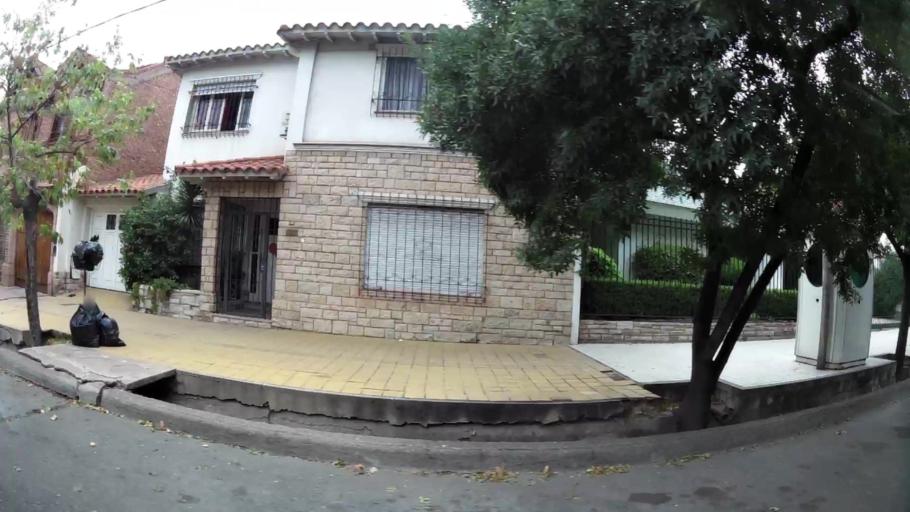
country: AR
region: Mendoza
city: Mendoza
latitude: -32.8875
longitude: -68.8536
